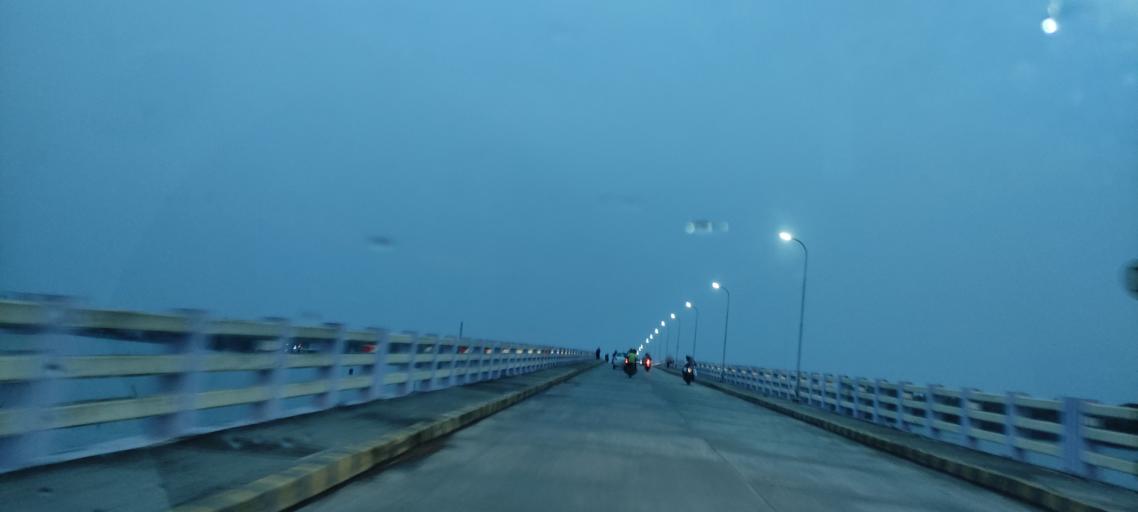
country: IN
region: Kerala
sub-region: Ernakulam
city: Cochin
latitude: 9.9263
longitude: 76.2876
